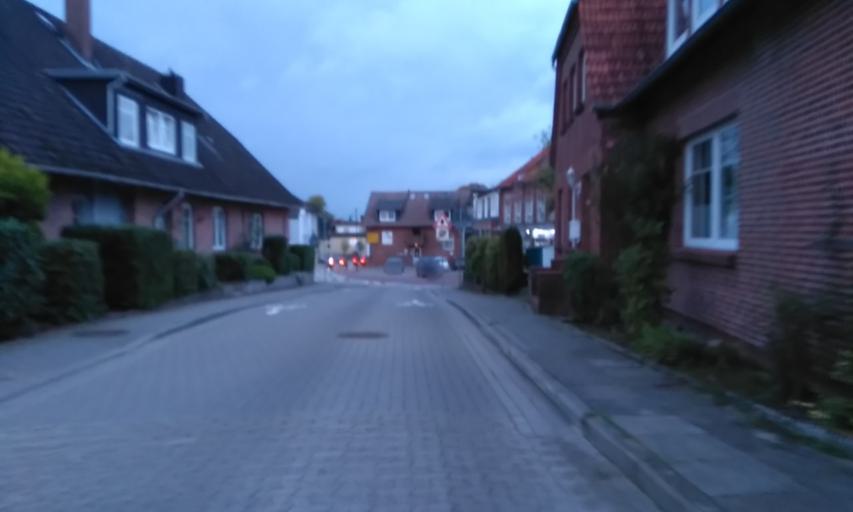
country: DE
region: Lower Saxony
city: Harsefeld
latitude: 53.4514
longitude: 9.5015
